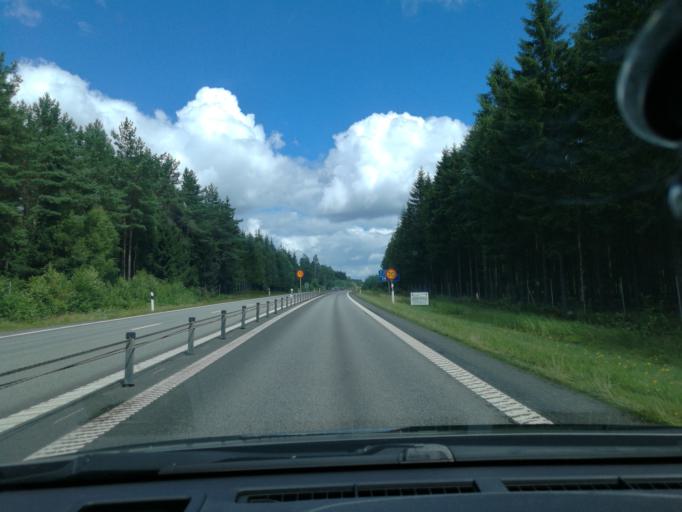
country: SE
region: Skane
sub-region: Hassleholms Kommun
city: Hassleholm
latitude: 56.1965
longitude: 13.8527
